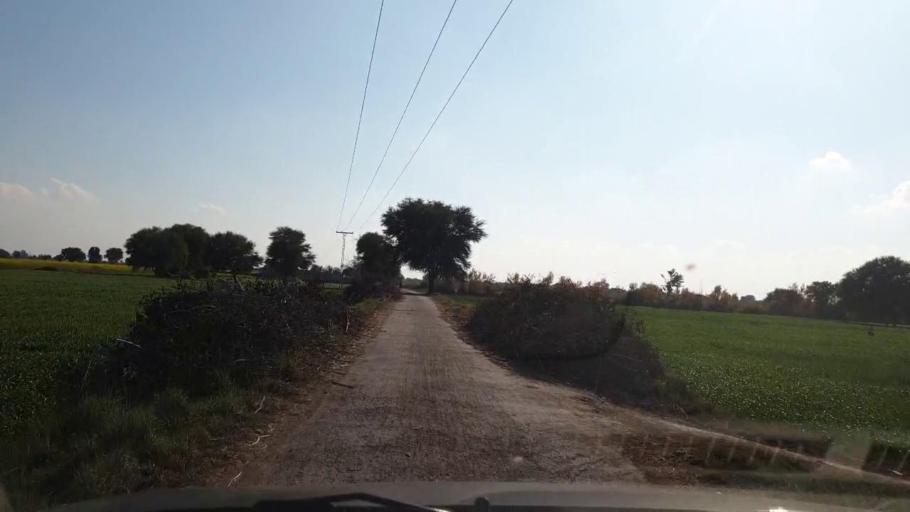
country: PK
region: Sindh
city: Sinjhoro
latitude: 25.9899
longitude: 68.7269
